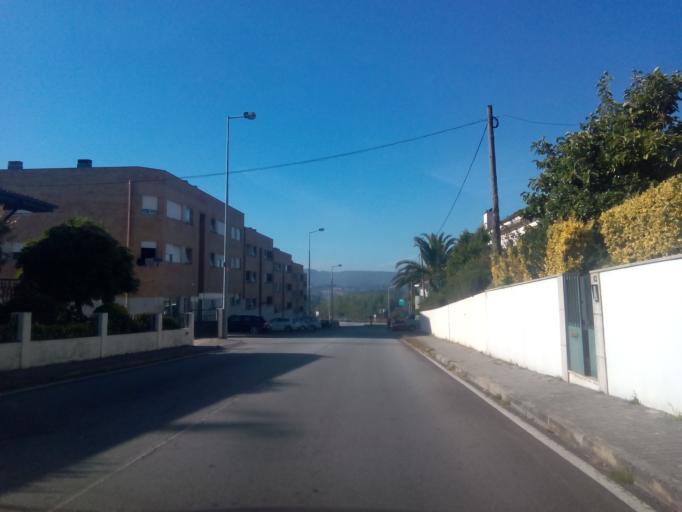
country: PT
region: Porto
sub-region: Paredes
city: Gandra
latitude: 41.1975
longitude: -8.4277
